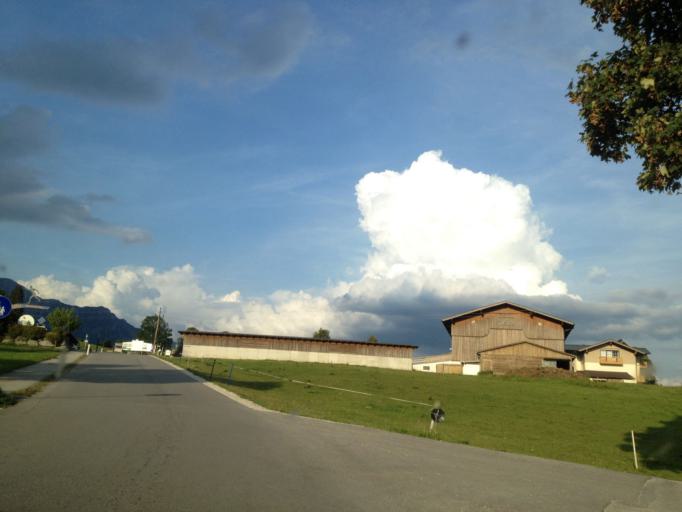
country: AT
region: Styria
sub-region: Politischer Bezirk Liezen
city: Schladming
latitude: 47.3989
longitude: 13.6185
